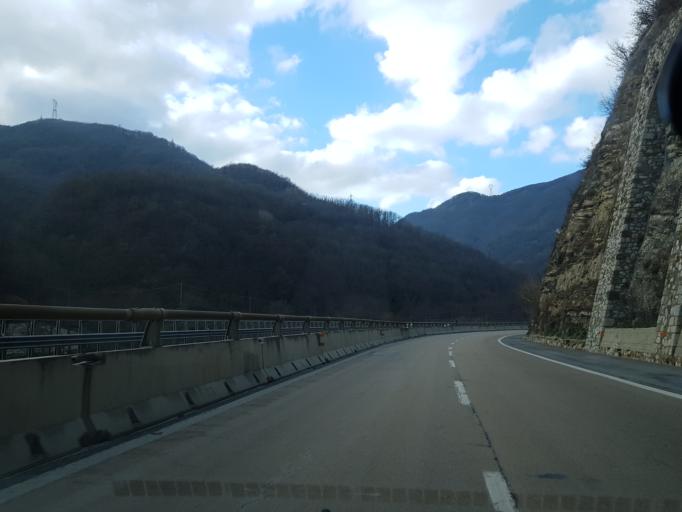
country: IT
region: Liguria
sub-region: Provincia di Genova
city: Ronco Scrivia
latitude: 44.6277
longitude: 8.9450
